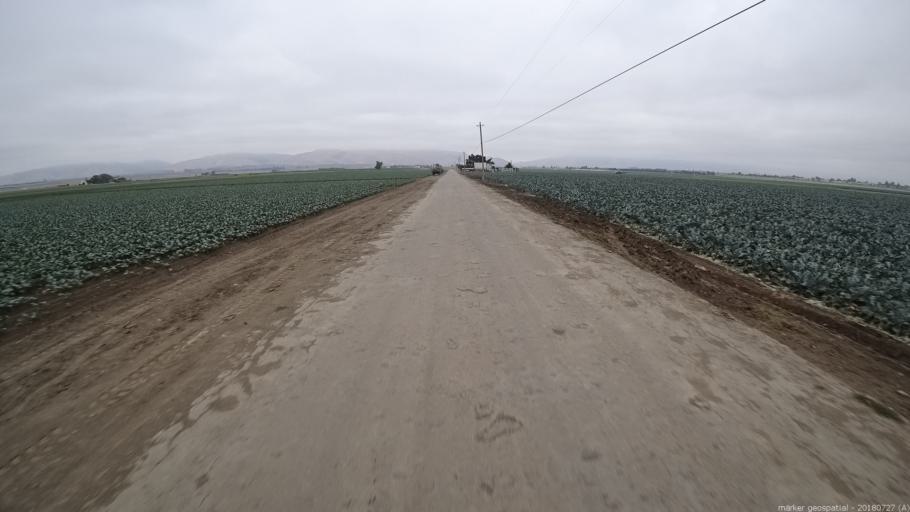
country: US
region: California
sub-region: Monterey County
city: Greenfield
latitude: 36.3174
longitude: -121.2137
